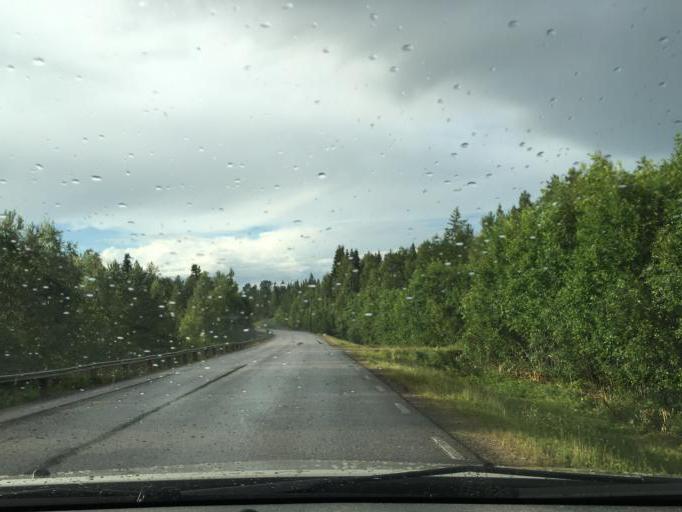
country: SE
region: Norrbotten
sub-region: Kalix Kommun
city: Rolfs
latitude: 65.9346
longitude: 22.8924
